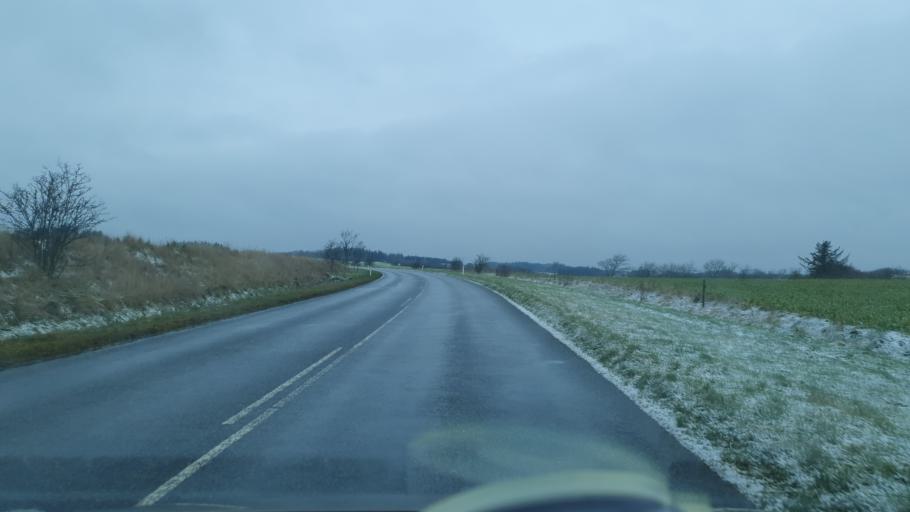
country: DK
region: North Denmark
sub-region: Jammerbugt Kommune
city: Brovst
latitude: 57.1239
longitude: 9.4900
